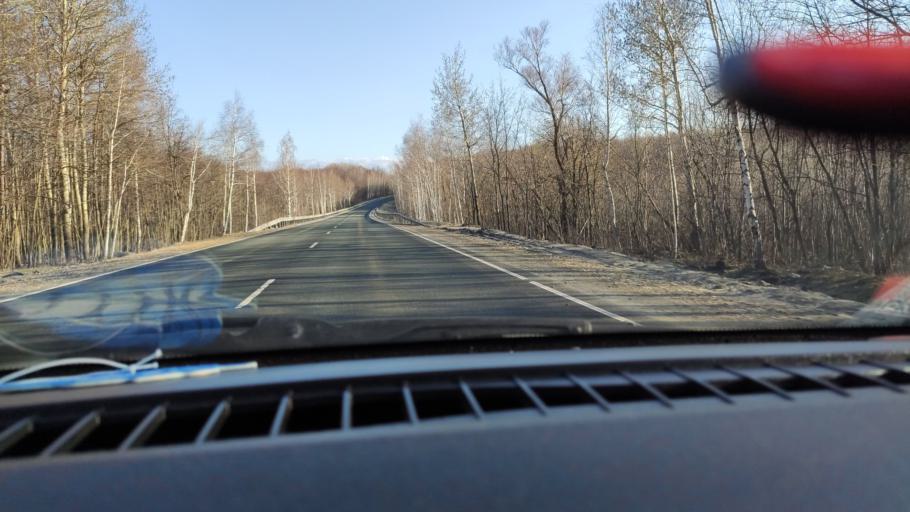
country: RU
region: Saratov
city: Khvalynsk
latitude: 52.4438
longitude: 48.0098
